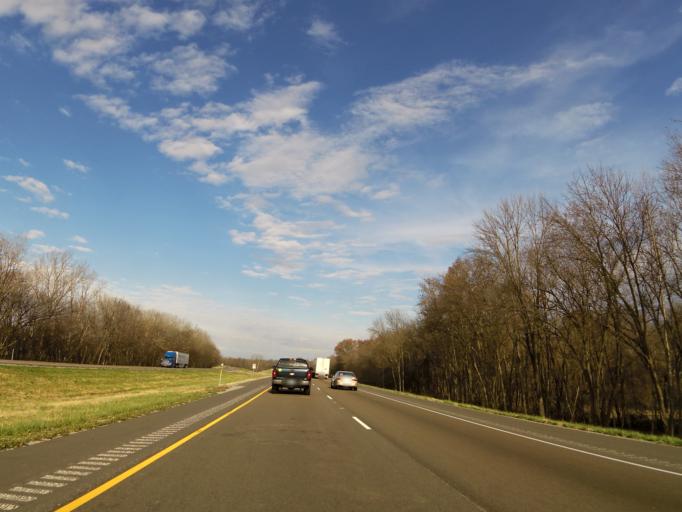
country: US
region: Illinois
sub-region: Washington County
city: Okawville
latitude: 38.4703
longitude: -89.5738
